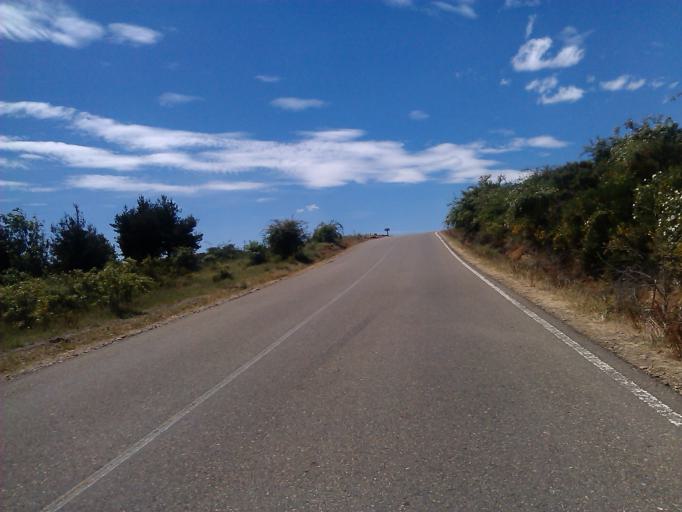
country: ES
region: Castille and Leon
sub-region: Provincia de Leon
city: Valverde de la Virgen
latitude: 42.5634
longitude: -5.6561
